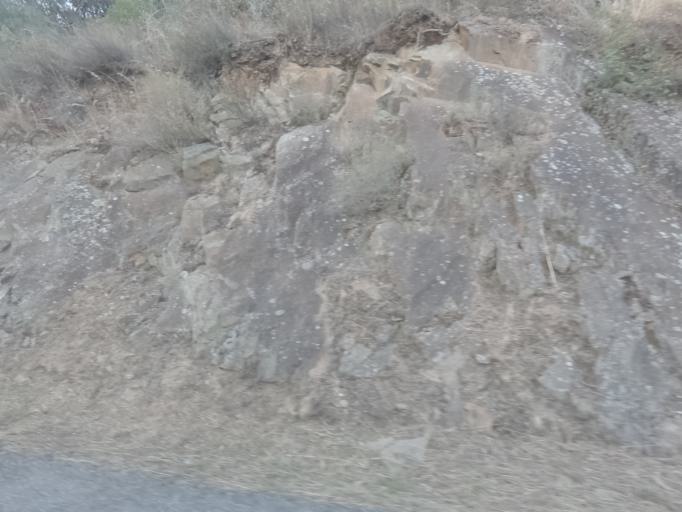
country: PT
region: Viseu
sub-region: Armamar
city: Armamar
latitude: 41.1795
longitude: -7.6888
